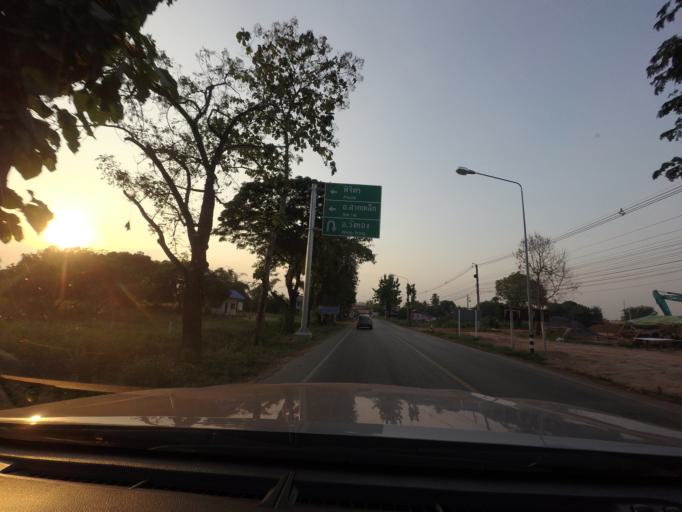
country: TH
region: Phitsanulok
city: Wang Thong
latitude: 16.7398
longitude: 100.4351
